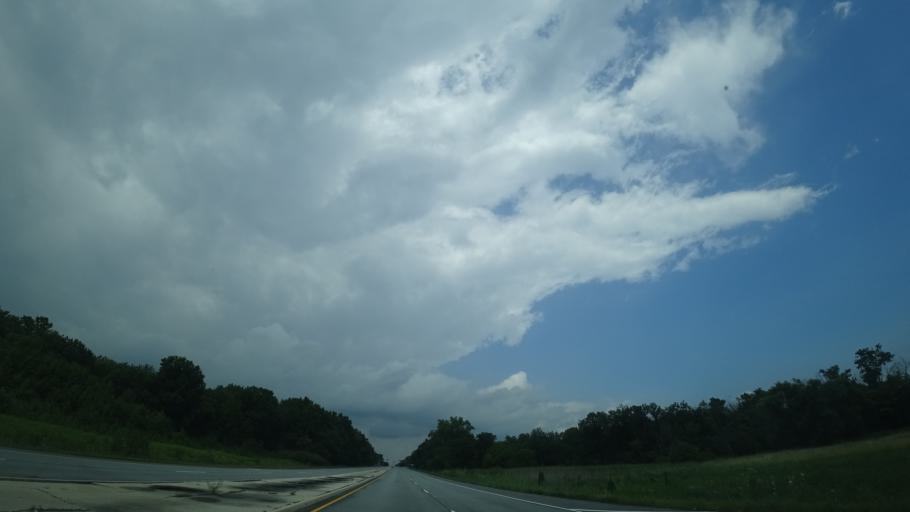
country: US
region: Illinois
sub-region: Cook County
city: Country Club Hills
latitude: 41.5386
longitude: -87.7326
